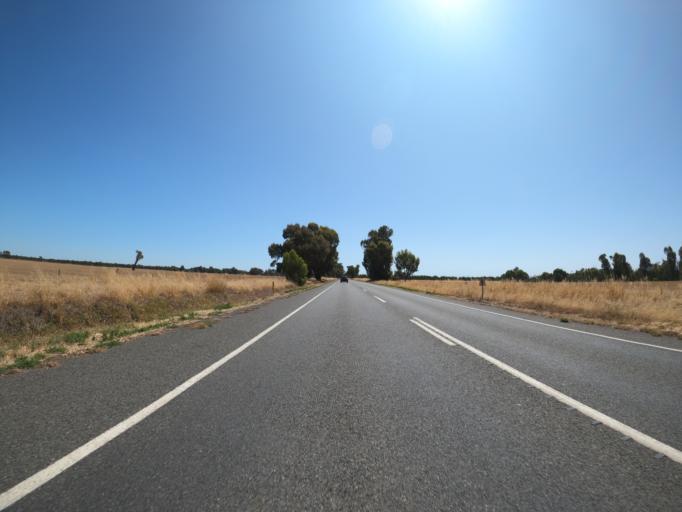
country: AU
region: Victoria
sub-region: Moira
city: Yarrawonga
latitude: -36.0224
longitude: 146.1352
